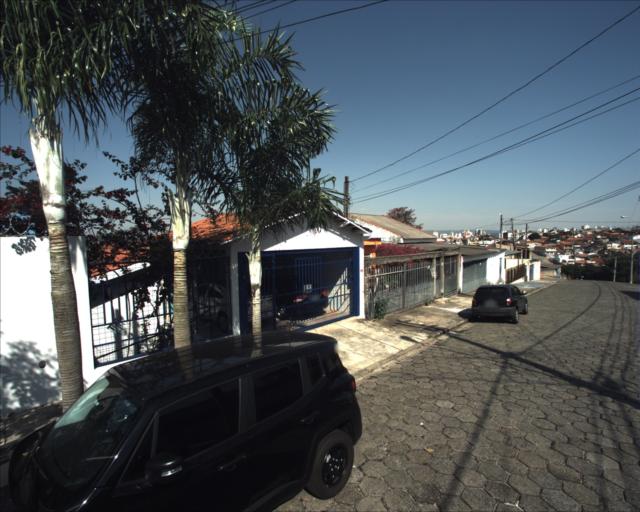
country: BR
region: Sao Paulo
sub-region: Sorocaba
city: Sorocaba
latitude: -23.4818
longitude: -47.4640
